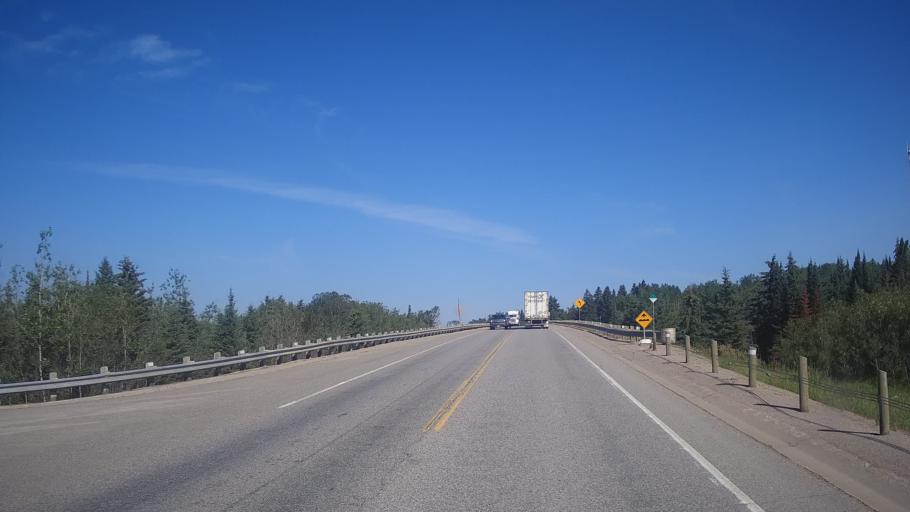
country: CA
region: Ontario
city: Dryden
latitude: 49.6890
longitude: -92.4958
